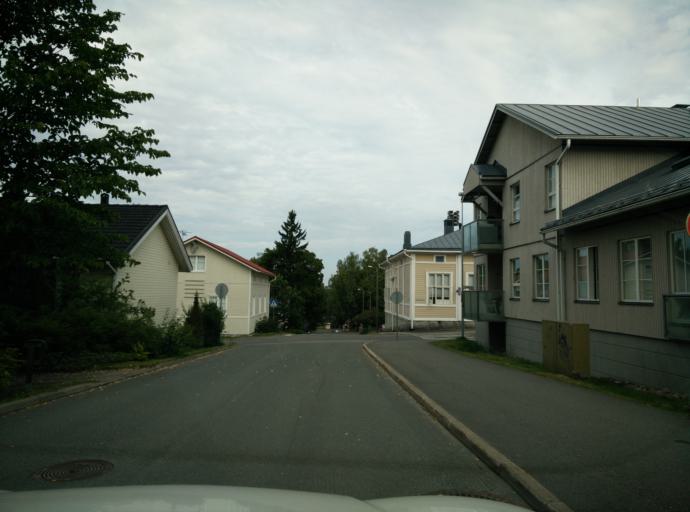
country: FI
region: Haeme
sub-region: Haemeenlinna
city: Haemeenlinna
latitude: 60.9911
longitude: 24.4454
